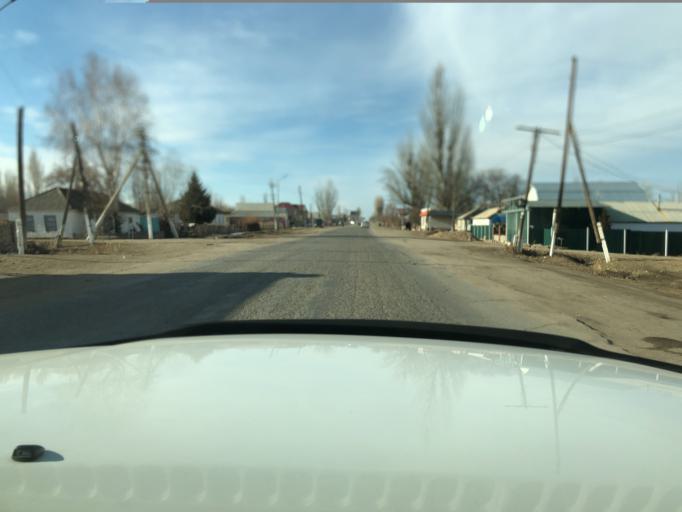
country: KG
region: Ysyk-Koel
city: Pokrovka
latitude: 42.3243
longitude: 77.9360
